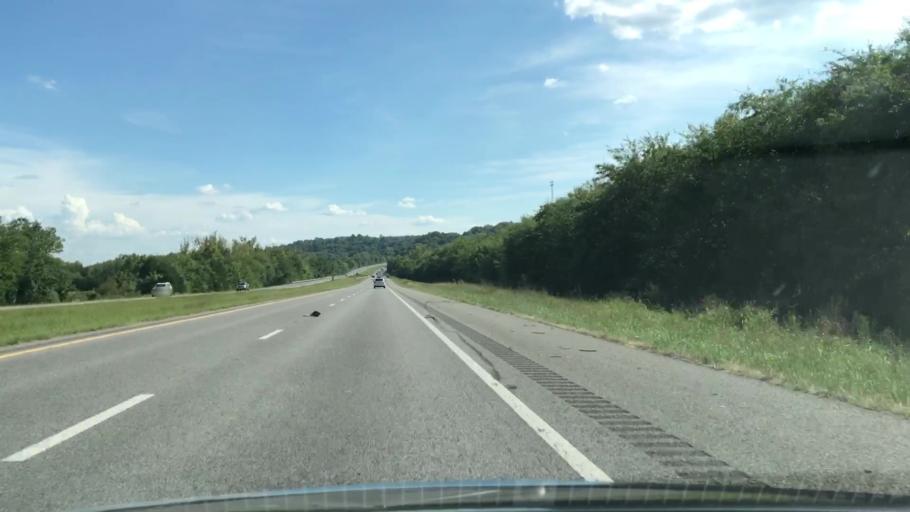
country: US
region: Alabama
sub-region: Limestone County
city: Ardmore
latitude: 35.1356
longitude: -86.8781
